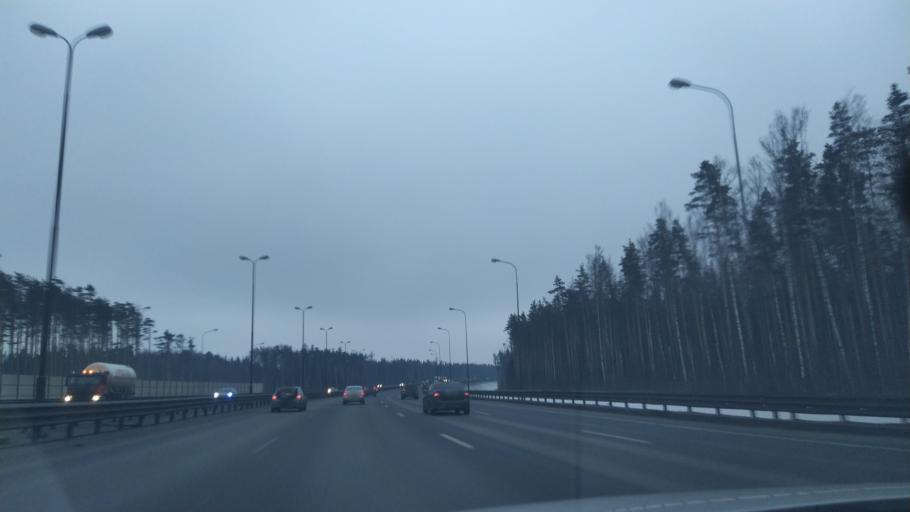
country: RU
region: St.-Petersburg
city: Krasnogvargeisky
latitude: 59.9704
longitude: 30.5493
